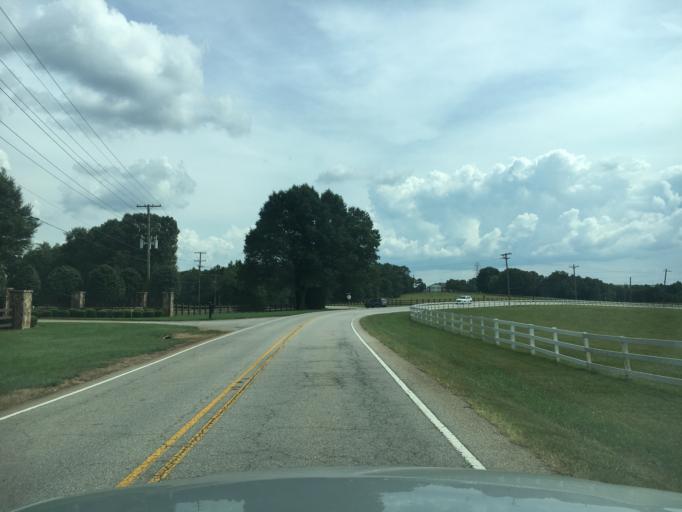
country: US
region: South Carolina
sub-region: Greenville County
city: Greer
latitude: 34.8775
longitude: -82.2405
